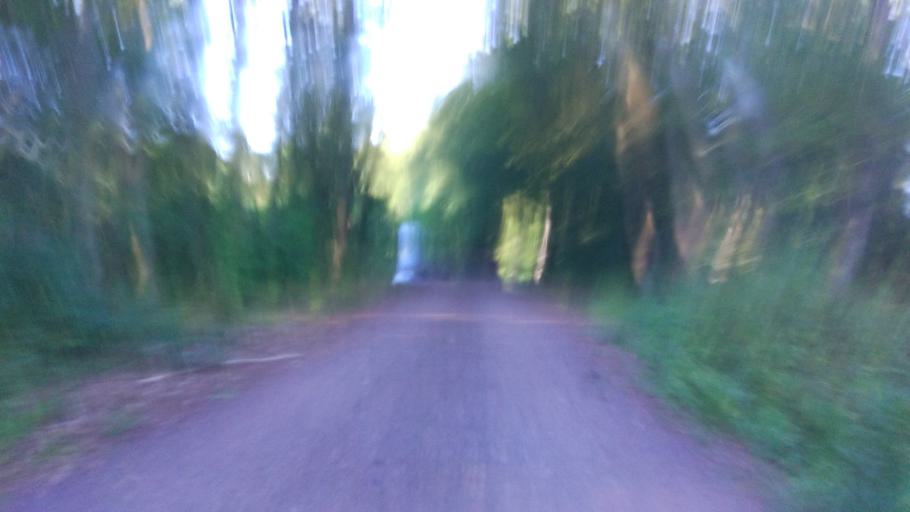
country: FR
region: Alsace
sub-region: Departement du Bas-Rhin
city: Kaltenhouse
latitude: 48.7748
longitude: 7.8223
